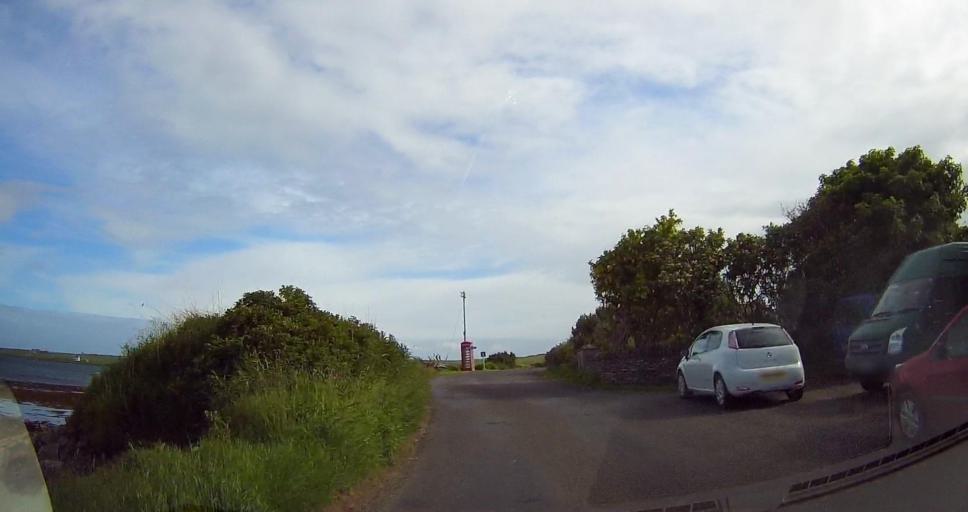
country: GB
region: Scotland
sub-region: Orkney Islands
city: Stromness
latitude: 58.8071
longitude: -3.2038
